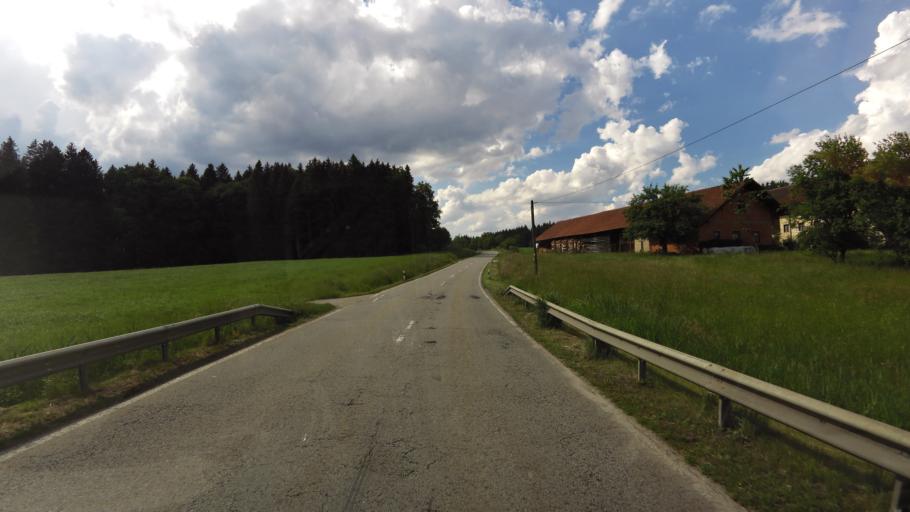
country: DE
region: Bavaria
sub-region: Upper Bavaria
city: Griesstatt
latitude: 47.9801
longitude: 12.2121
